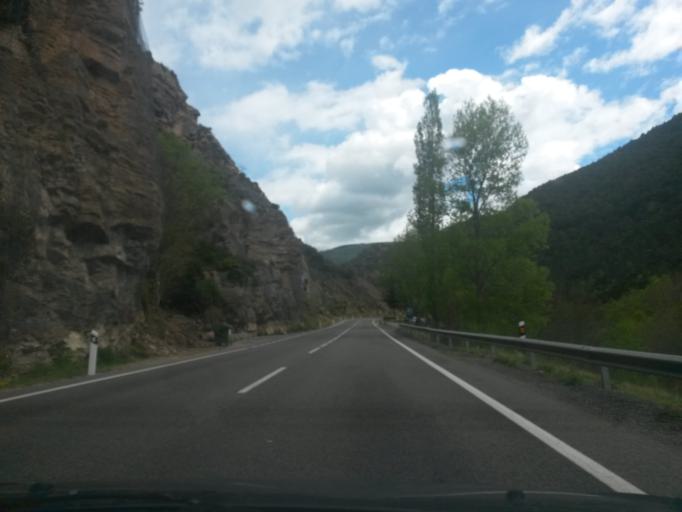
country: ES
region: Catalonia
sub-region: Provincia de Lleida
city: Alas i Cerc
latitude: 42.3587
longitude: 1.5462
